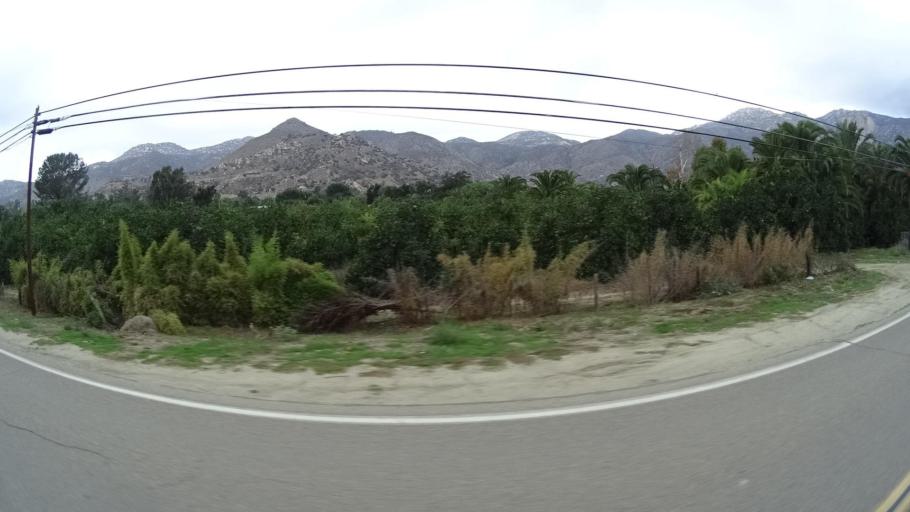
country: US
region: California
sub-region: San Diego County
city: Harbison Canyon
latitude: 32.8835
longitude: -116.8547
